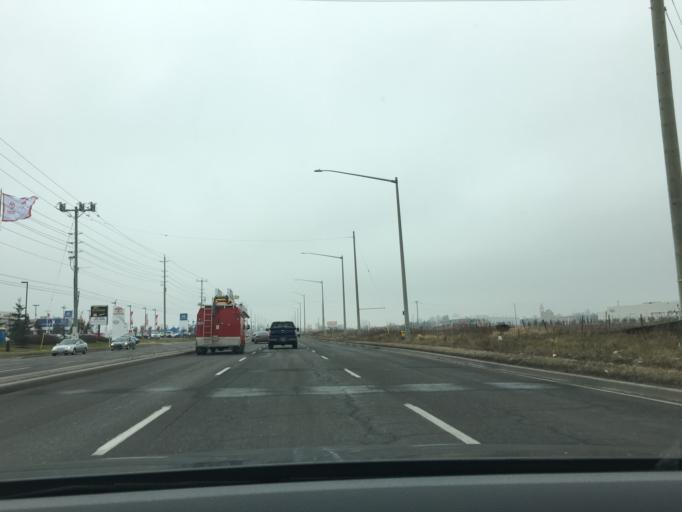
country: CA
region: Ontario
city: Innisfil
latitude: 44.3321
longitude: -79.6997
